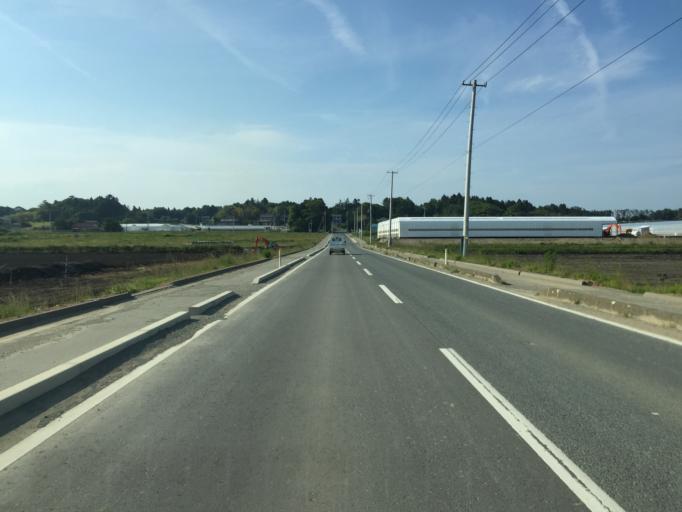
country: JP
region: Fukushima
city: Namie
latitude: 37.7038
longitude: 141.0057
